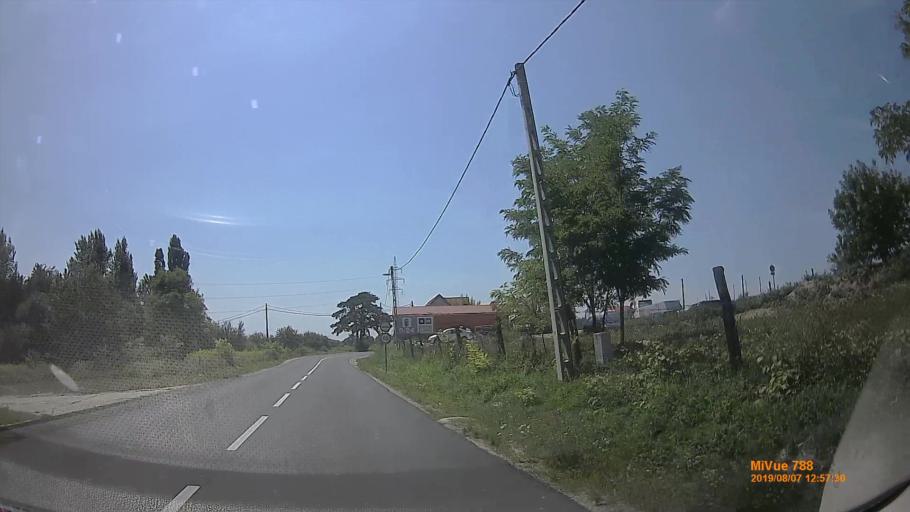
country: HU
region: Zala
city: Keszthely
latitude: 46.7880
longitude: 17.2573
